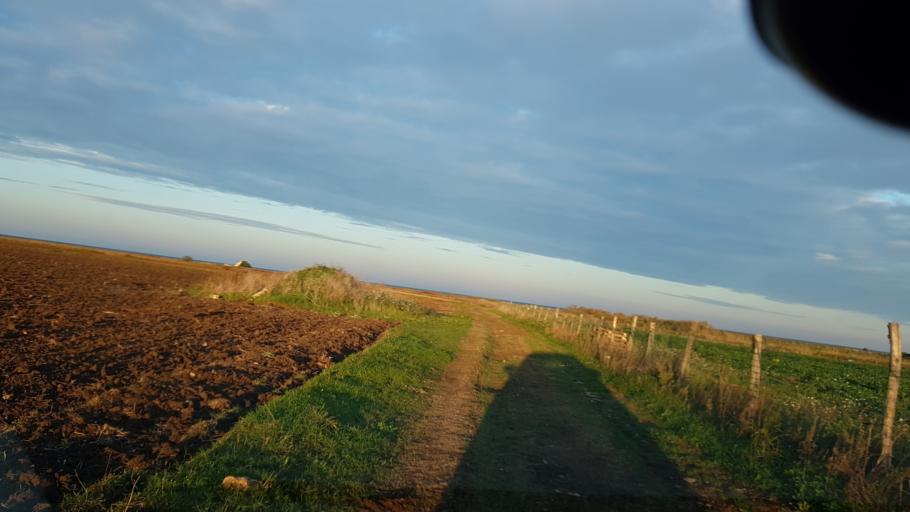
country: IT
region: Apulia
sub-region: Provincia di Brindisi
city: La Rosa
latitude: 40.6107
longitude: 18.0156
